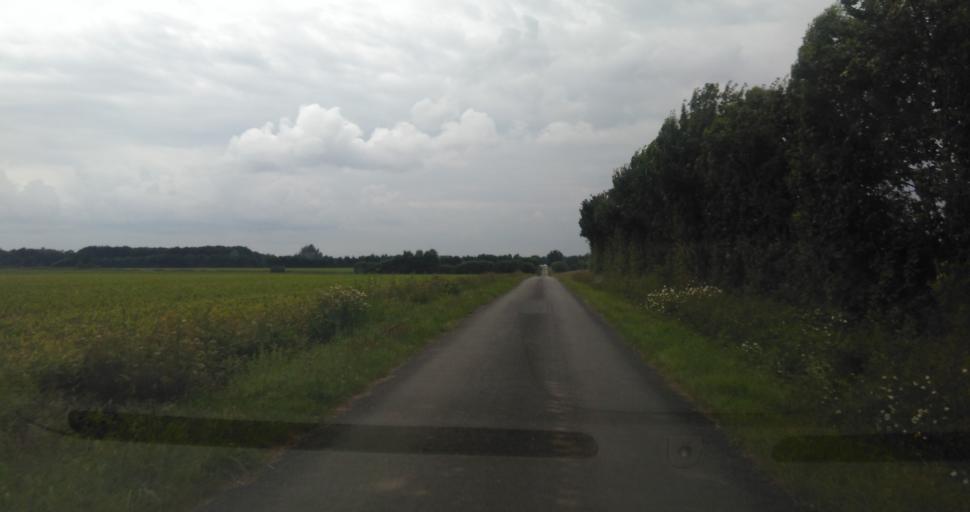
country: FR
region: Pays de la Loire
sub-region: Departement de la Vendee
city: Saint-Georges-de-Montaigu
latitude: 46.9268
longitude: -1.3183
